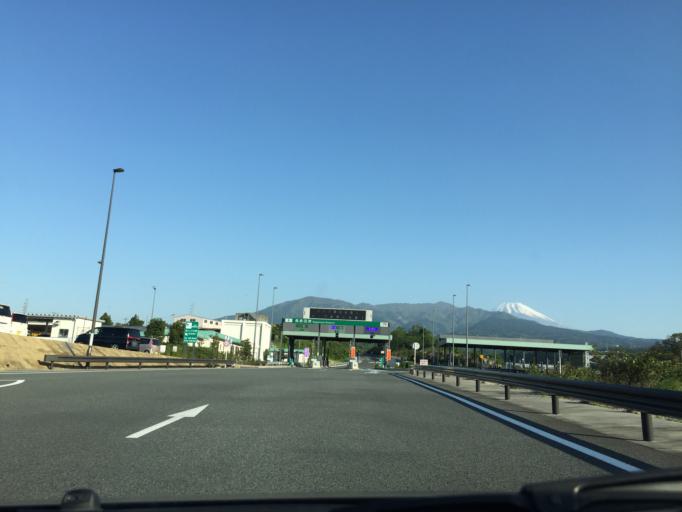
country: JP
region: Shizuoka
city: Numazu
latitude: 35.1502
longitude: 138.8744
